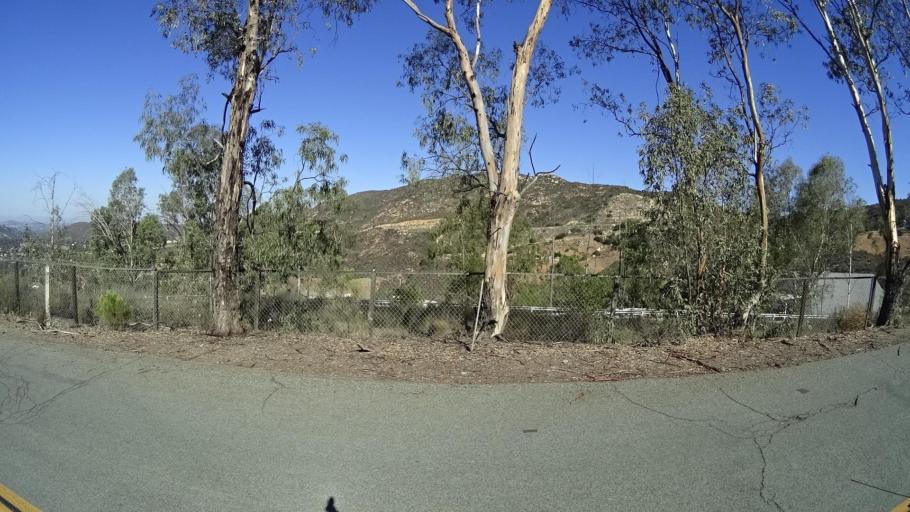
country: US
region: California
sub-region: San Diego County
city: Jamul
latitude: 32.7299
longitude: -116.8324
